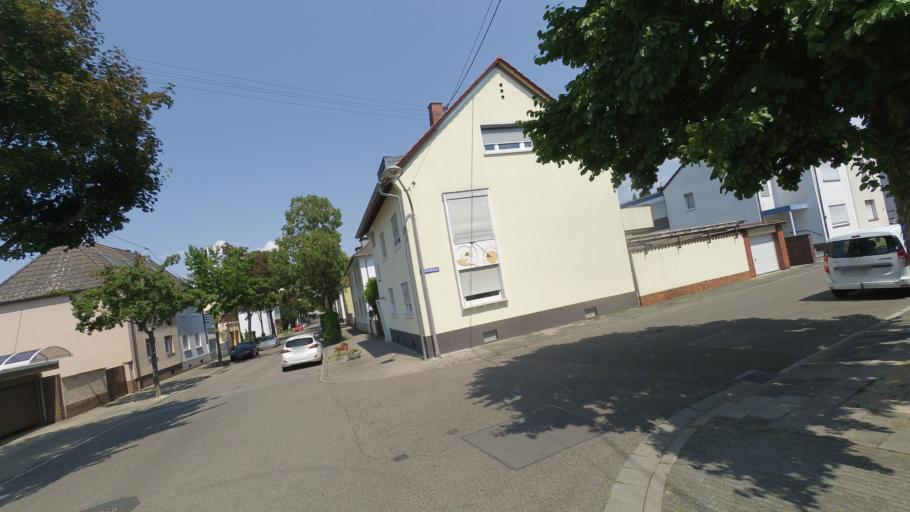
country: DE
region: Rheinland-Pfalz
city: Frankenthal
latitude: 49.5269
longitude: 8.3926
